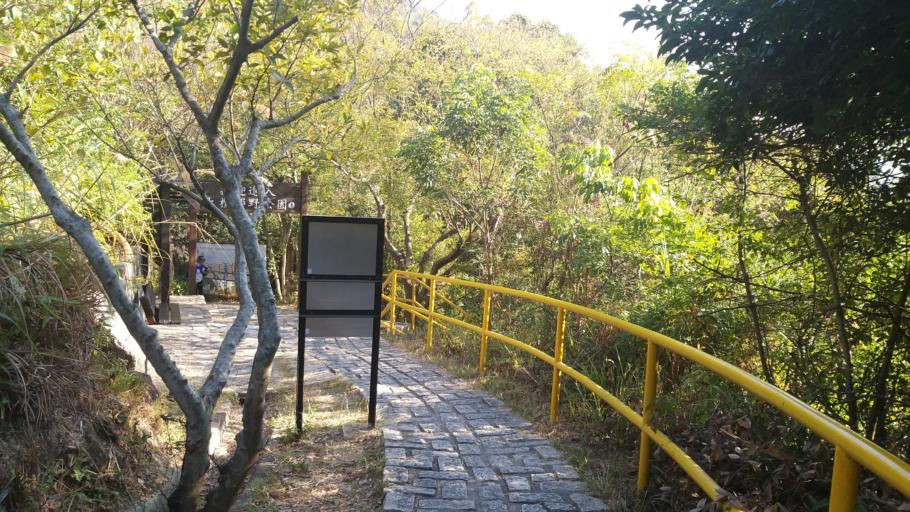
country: HK
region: Tuen Mun
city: Tuen Mun
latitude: 22.3947
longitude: 113.9824
